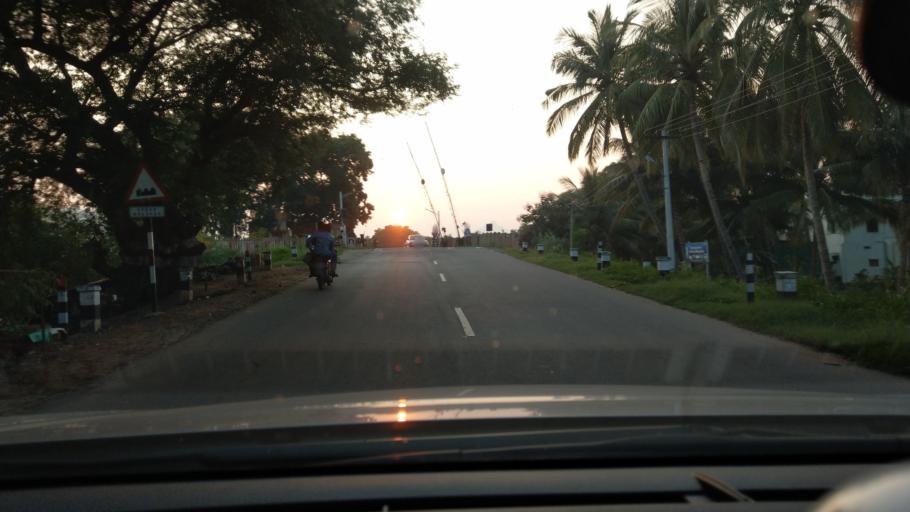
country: IN
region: Tamil Nadu
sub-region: Salem
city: Attur
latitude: 11.5987
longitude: 78.5762
